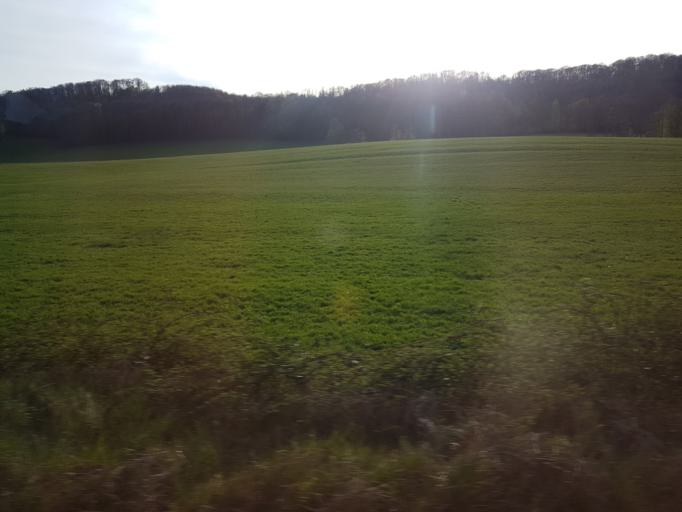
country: FR
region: Franche-Comte
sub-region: Departement de la Haute-Saone
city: Vaivre-et-Montoille
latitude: 47.6350
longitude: 6.1003
